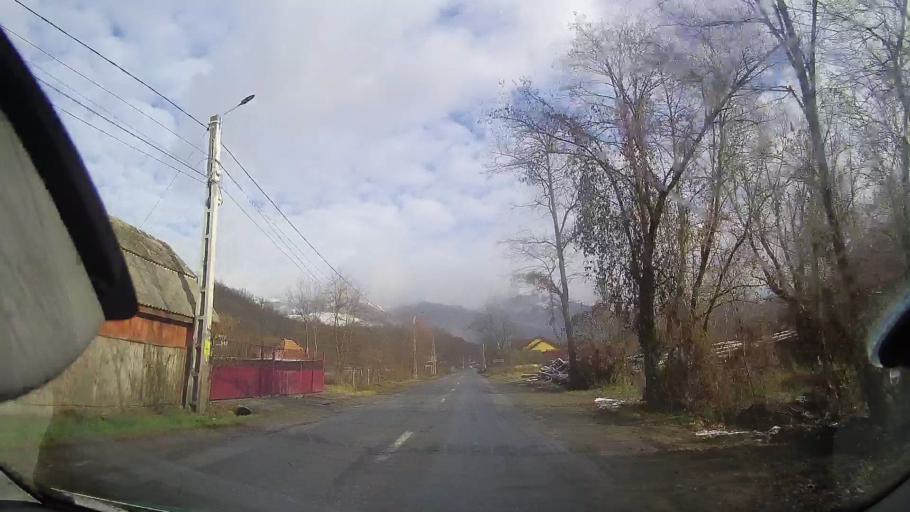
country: RO
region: Alba
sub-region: Comuna Lupsa
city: Lupsa
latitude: 46.3763
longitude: 23.2180
